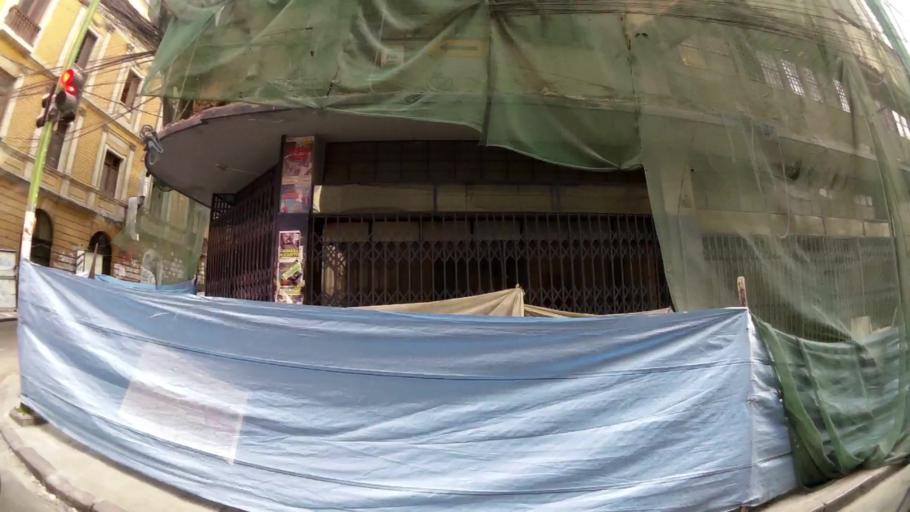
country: BO
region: La Paz
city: La Paz
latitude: -16.4983
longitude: -68.1327
